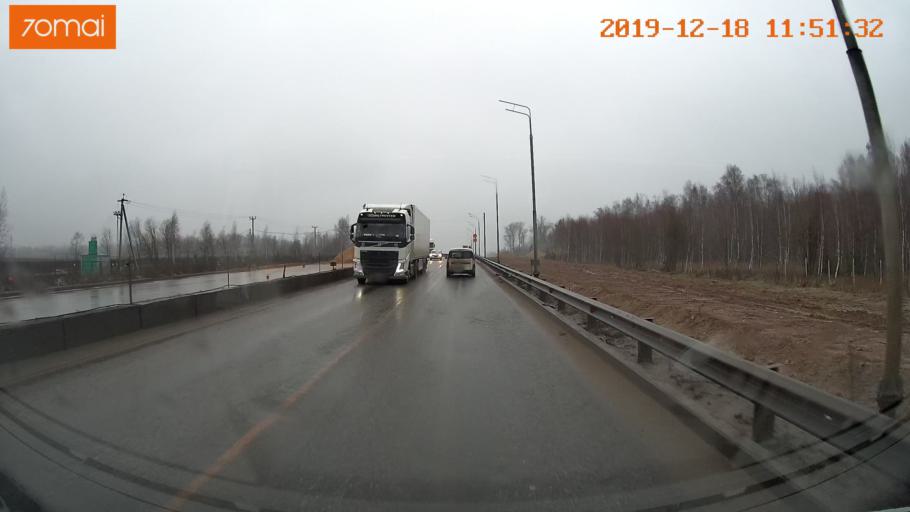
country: RU
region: Moskovskaya
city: Yershovo
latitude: 55.7940
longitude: 36.9219
